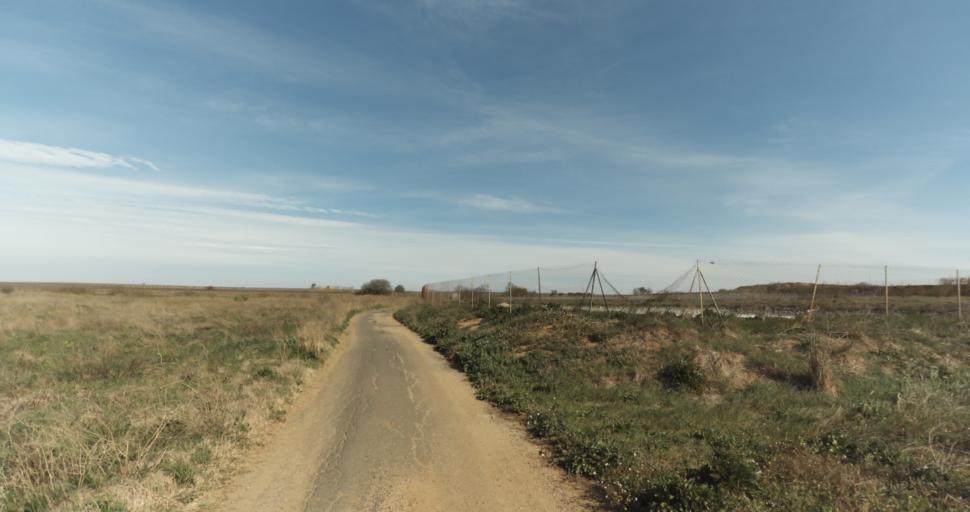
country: FR
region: Languedoc-Roussillon
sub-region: Departement de l'Herault
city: Marseillan
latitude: 43.3513
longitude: 3.5042
